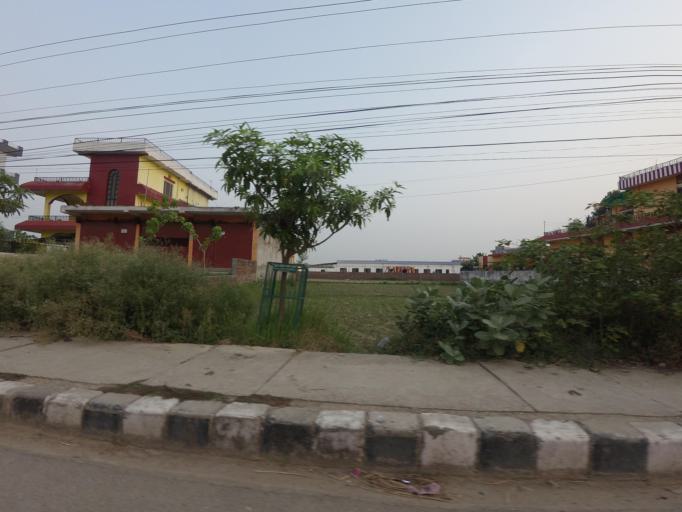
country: NP
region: Western Region
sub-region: Lumbini Zone
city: Bhairahawa
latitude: 27.5110
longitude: 83.4626
